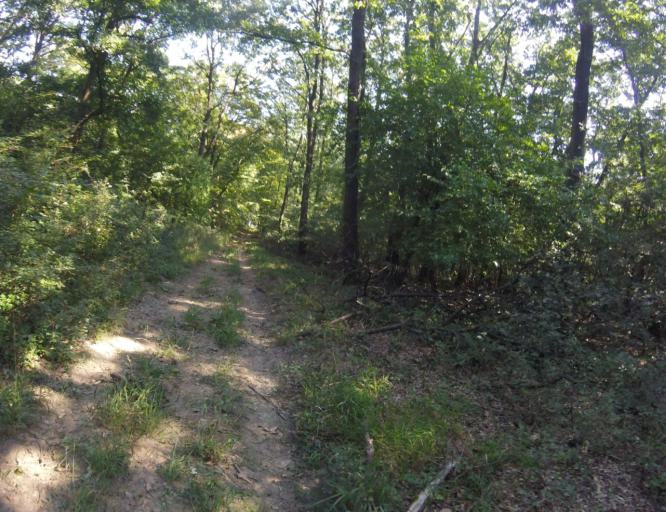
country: HU
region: Fejer
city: Lovasbereny
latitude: 47.2738
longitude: 18.5920
